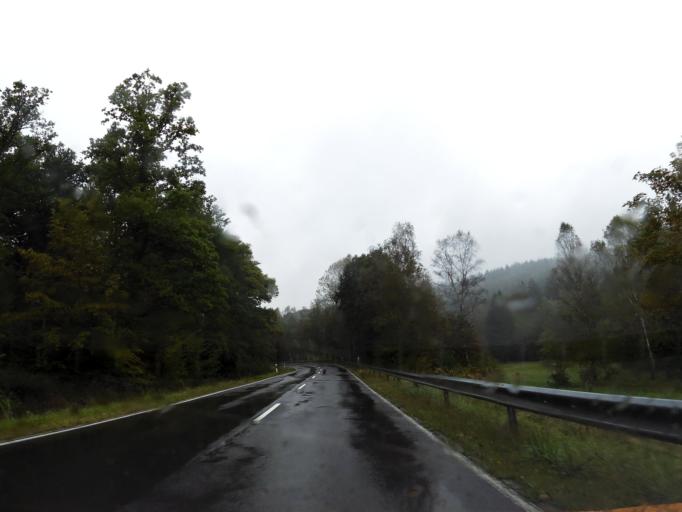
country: DE
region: Rheinland-Pfalz
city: Munchwald
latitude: 49.9258
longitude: 7.6540
